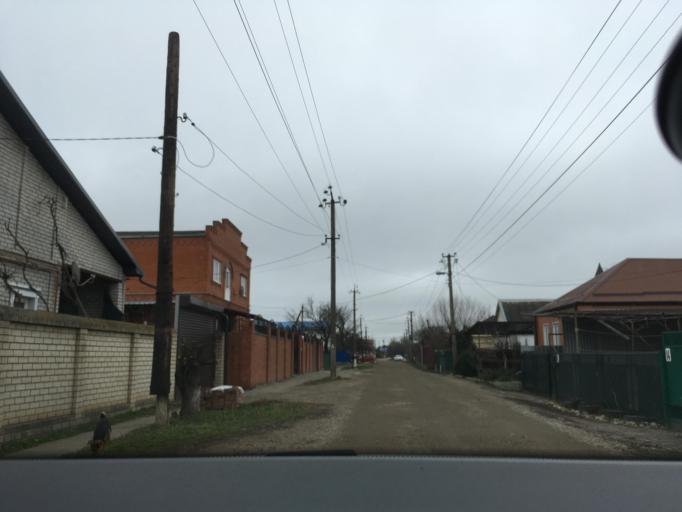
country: RU
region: Krasnodarskiy
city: Kushchevskaya
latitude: 46.5762
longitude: 39.6221
